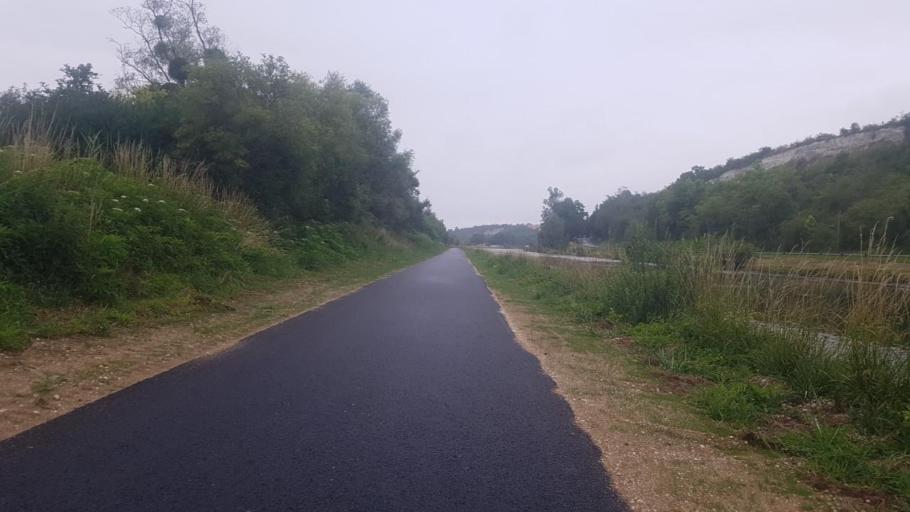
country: FR
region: Champagne-Ardenne
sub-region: Departement de la Marne
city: Vitry-le-Francois
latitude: 48.7848
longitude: 4.5366
